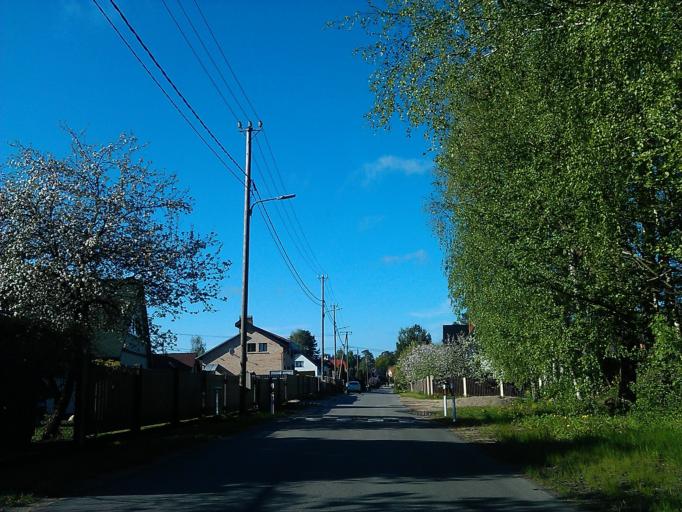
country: LV
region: Riga
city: Bergi
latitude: 57.0112
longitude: 24.2690
